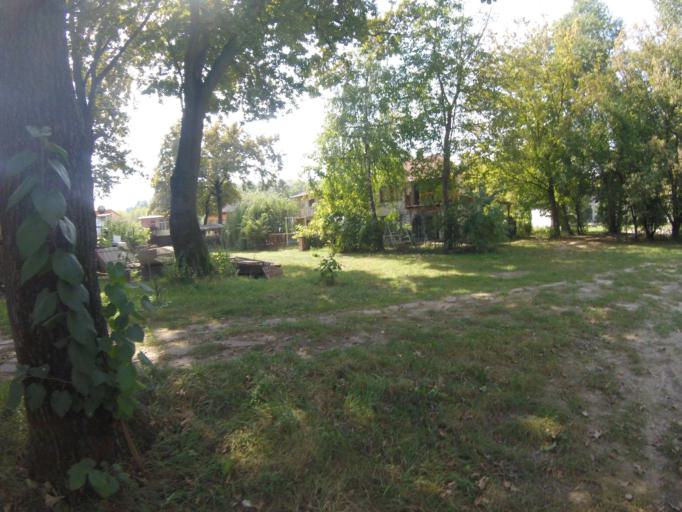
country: HU
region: Bacs-Kiskun
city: Baja
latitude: 46.1970
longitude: 18.9201
